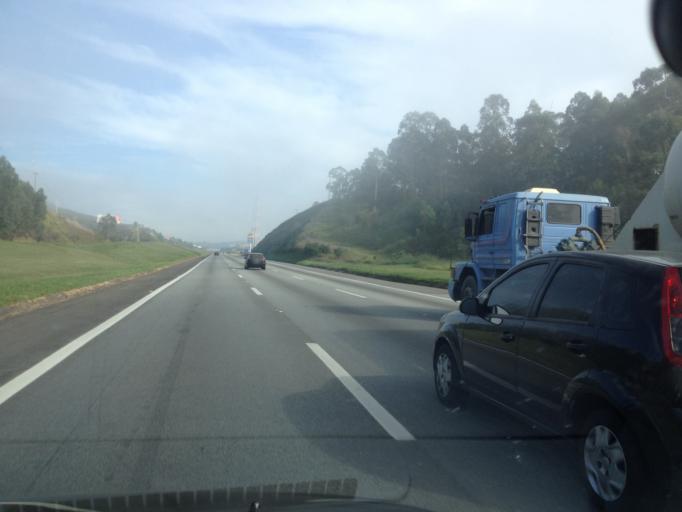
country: BR
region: Sao Paulo
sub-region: Sao Roque
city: Sao Roque
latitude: -23.4214
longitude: -47.1724
